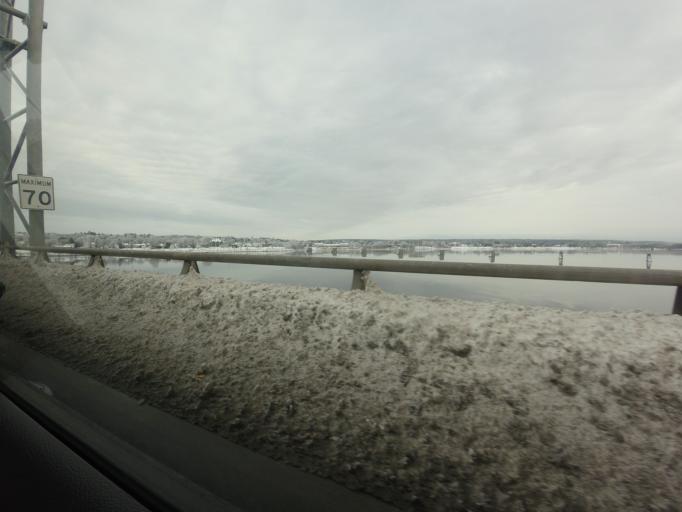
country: CA
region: New Brunswick
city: Fredericton
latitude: 45.9666
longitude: -66.6435
